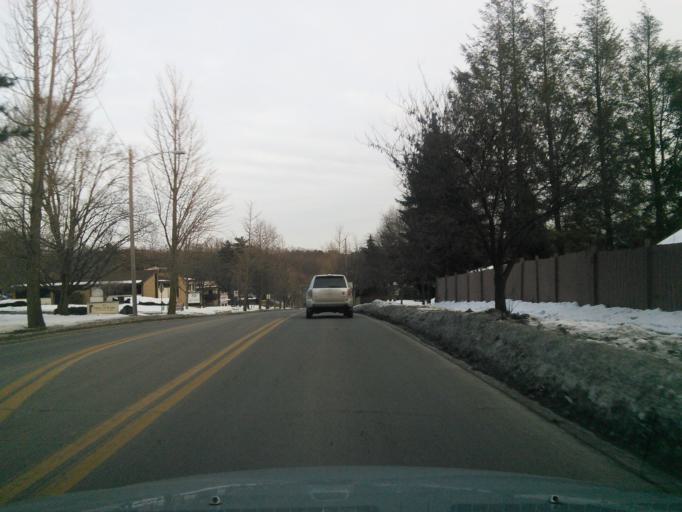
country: US
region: Pennsylvania
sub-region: Centre County
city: State College
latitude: 40.7980
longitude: -77.8460
